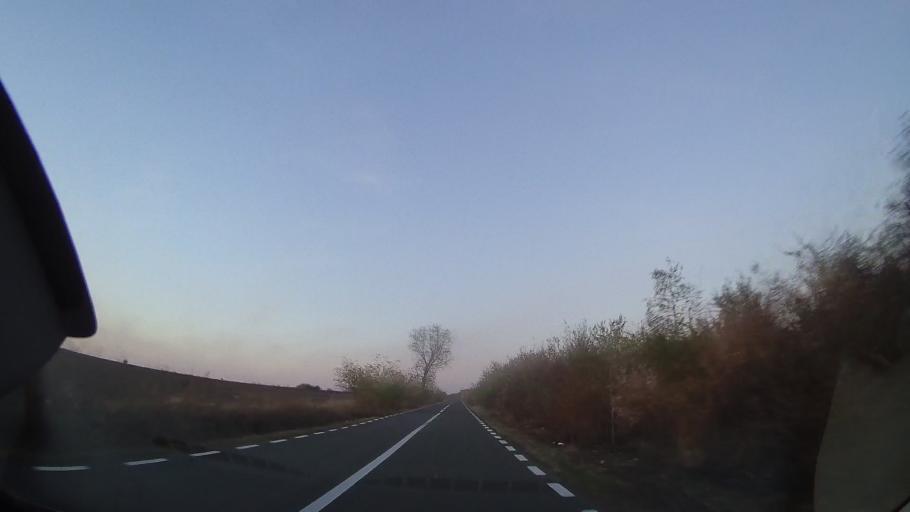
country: RO
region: Constanta
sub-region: Comuna Cobadin
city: Cobadin
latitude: 44.0313
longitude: 28.2610
